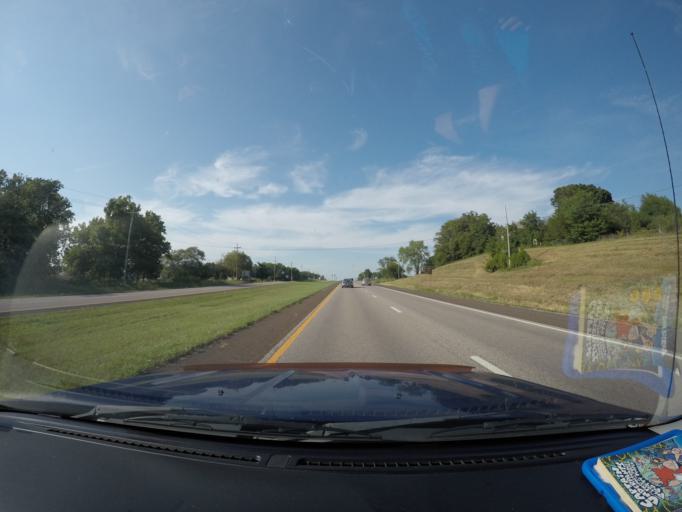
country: US
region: Kansas
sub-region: Leavenworth County
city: Lansing
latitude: 39.2004
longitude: -94.9002
